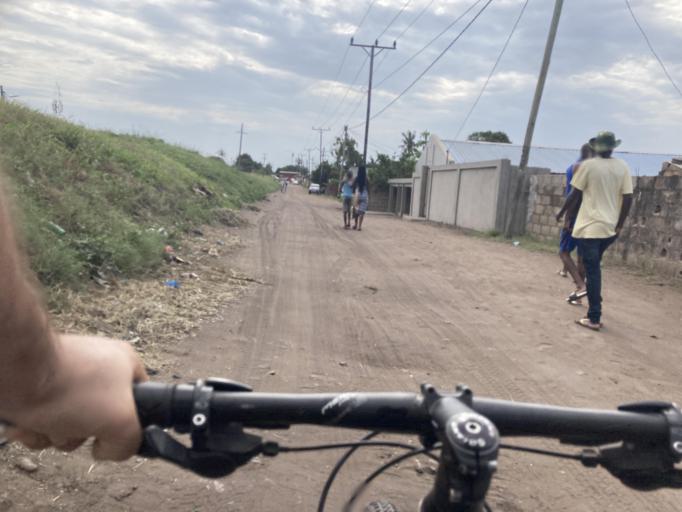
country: MZ
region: Maputo City
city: Maputo
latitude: -25.9267
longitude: 32.5876
